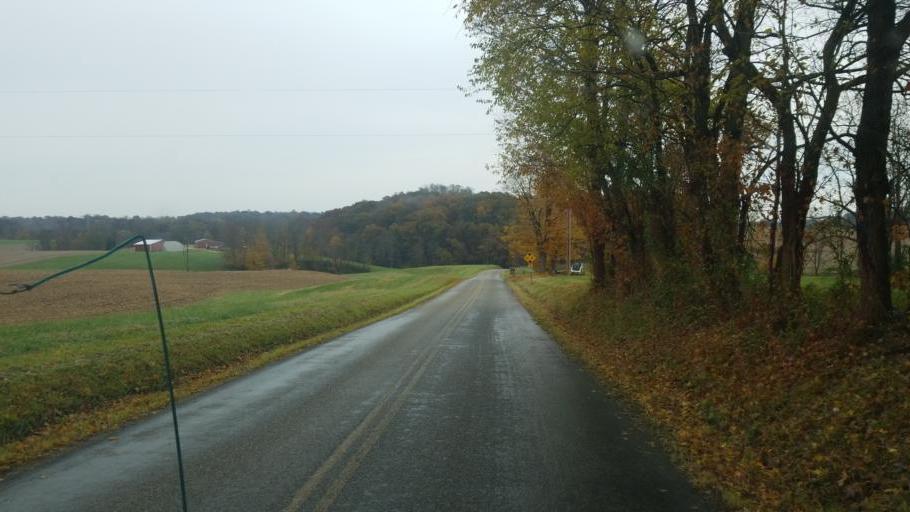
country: US
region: Ohio
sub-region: Washington County
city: Beverly
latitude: 39.5539
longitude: -81.6846
